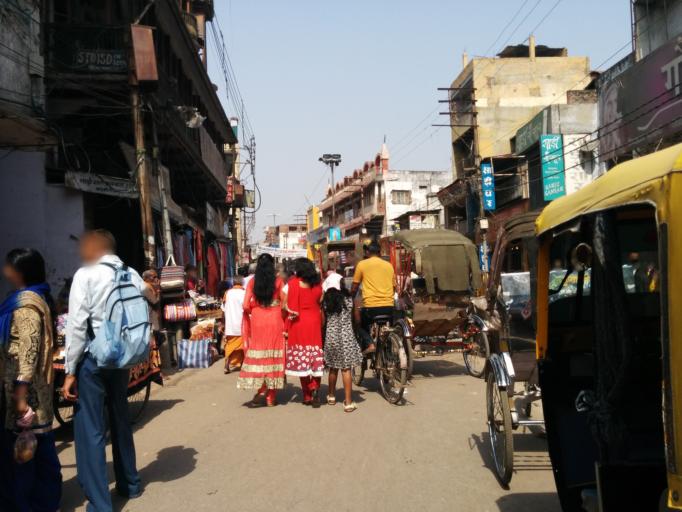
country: IN
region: Uttar Pradesh
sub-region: Varanasi
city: Varanasi
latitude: 25.3088
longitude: 83.0092
